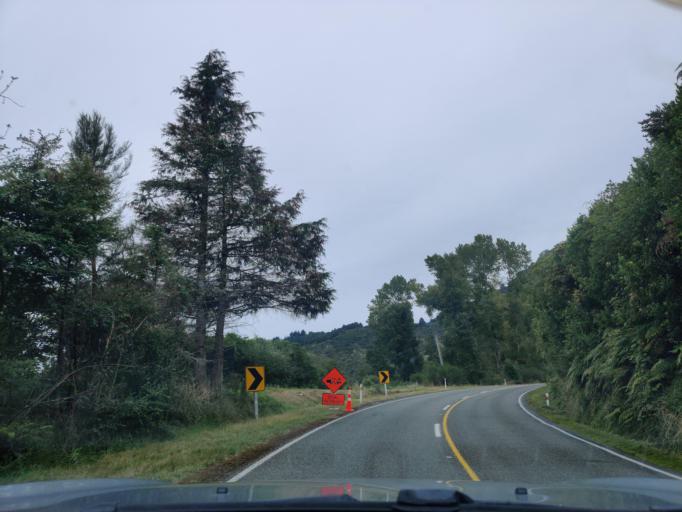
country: NZ
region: West Coast
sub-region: Buller District
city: Westport
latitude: -41.8417
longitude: 171.9070
